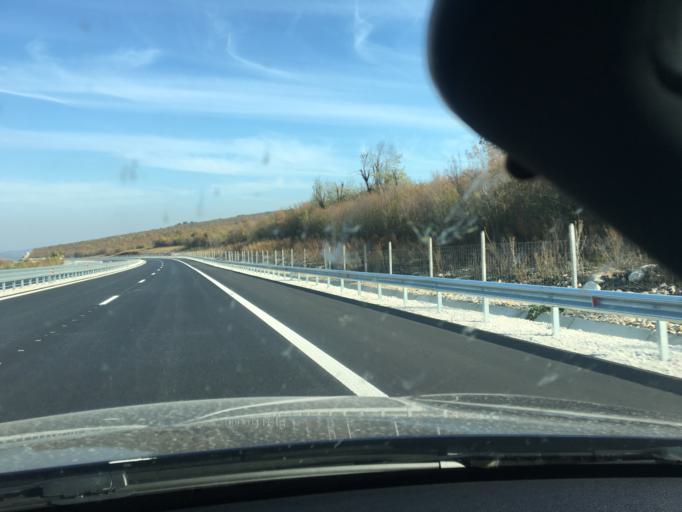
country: BG
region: Lovech
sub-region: Obshtina Yablanitsa
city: Yablanitsa
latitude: 43.0495
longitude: 24.1488
